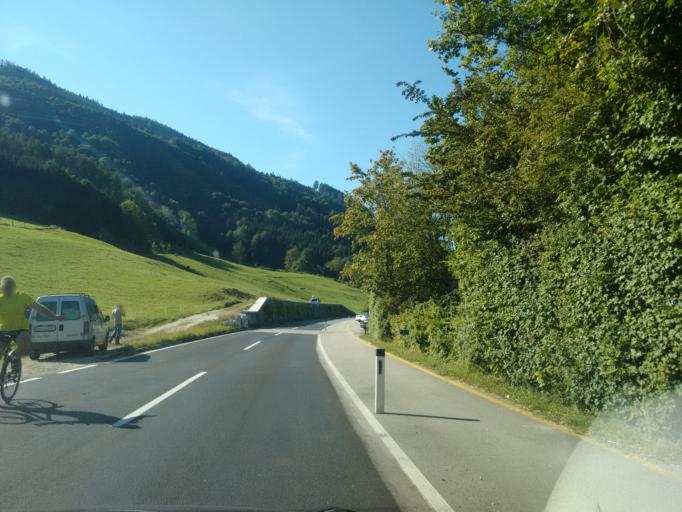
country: AT
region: Upper Austria
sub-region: Politischer Bezirk Vocklabruck
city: Steinbach am Attersee
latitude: 47.8724
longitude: 13.5679
